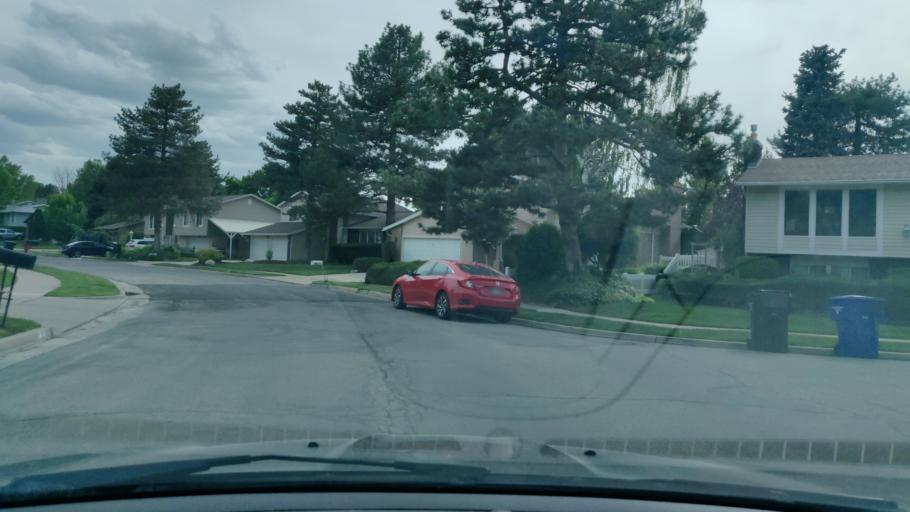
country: US
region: Utah
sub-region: Salt Lake County
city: Cottonwood Heights
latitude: 40.6199
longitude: -111.8036
